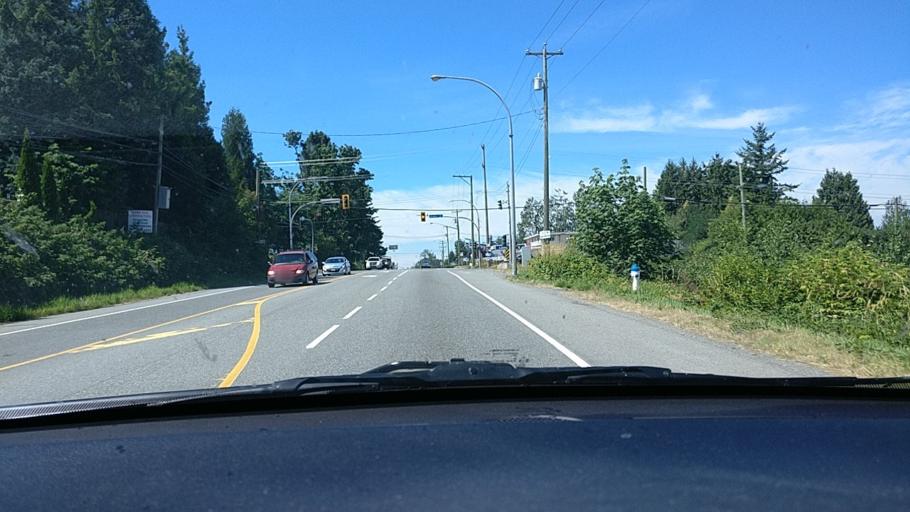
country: CA
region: British Columbia
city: Aldergrove
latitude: 49.0571
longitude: -122.4250
